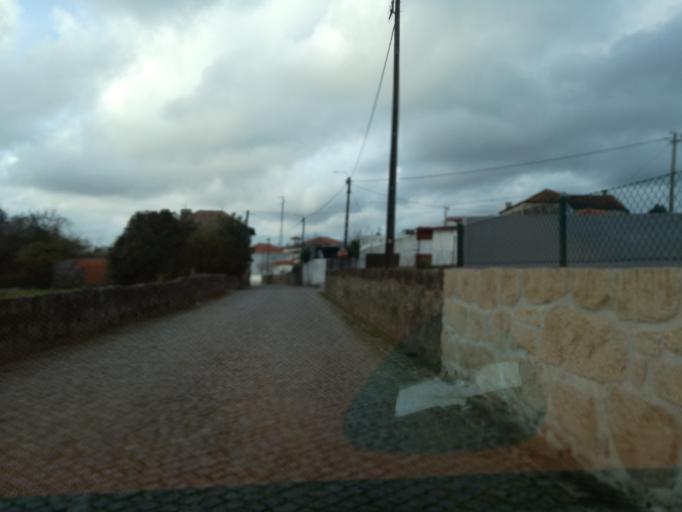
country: PT
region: Porto
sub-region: Maia
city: Nogueira
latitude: 41.2565
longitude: -8.6011
